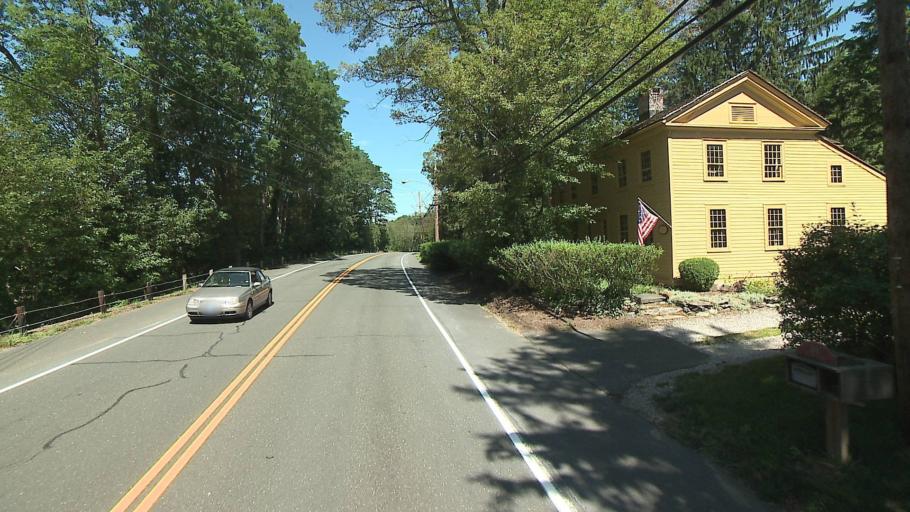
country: US
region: Connecticut
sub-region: Hartford County
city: Collinsville
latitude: 41.8220
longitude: -72.9238
